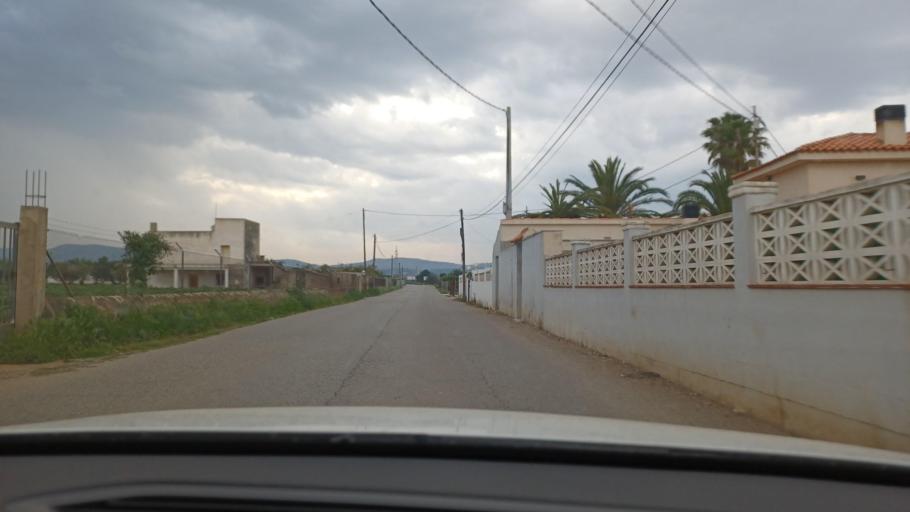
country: ES
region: Valencia
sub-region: Provincia de Castello
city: Benicarlo
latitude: 40.4065
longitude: 0.4010
